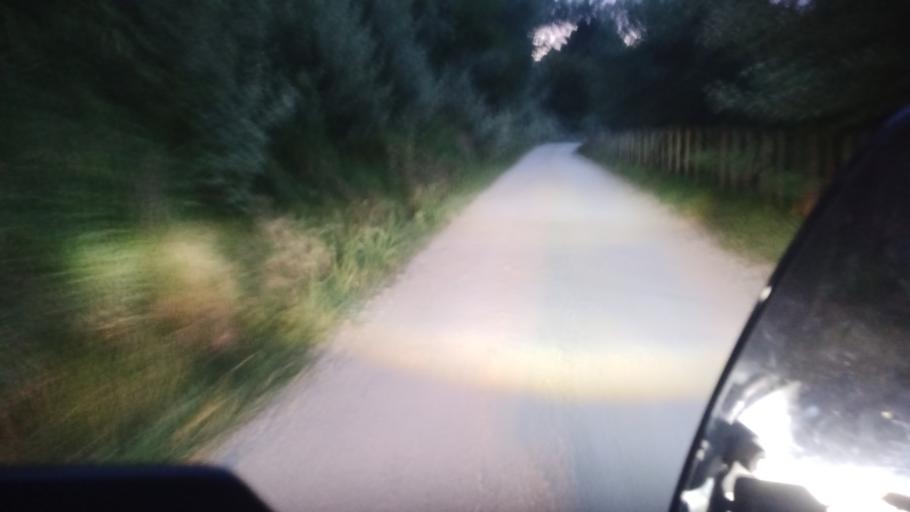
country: NZ
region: Gisborne
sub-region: Gisborne District
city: Gisborne
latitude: -38.4929
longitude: 177.9598
